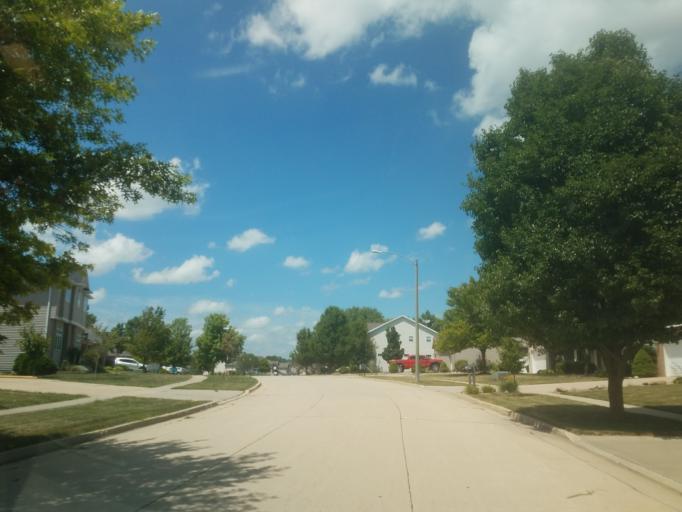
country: US
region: Illinois
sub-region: McLean County
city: Bloomington
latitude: 40.4501
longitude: -89.0303
